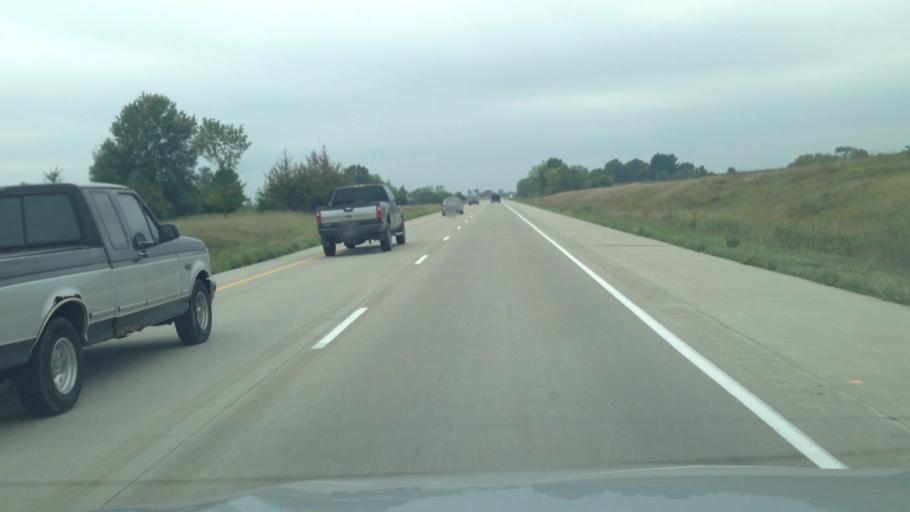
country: US
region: Iowa
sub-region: Decatur County
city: Lamoni
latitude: 40.5974
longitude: -93.9152
